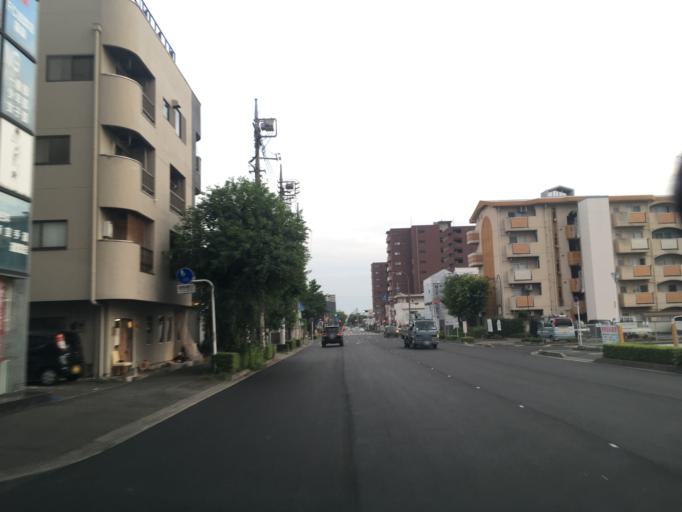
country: JP
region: Gunma
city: Maebashi-shi
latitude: 36.3838
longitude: 139.0764
